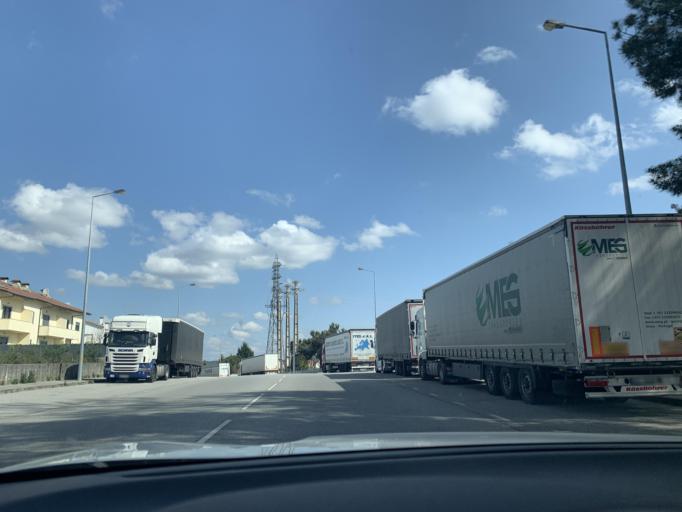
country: PT
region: Viseu
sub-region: Viseu
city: Rio de Loba
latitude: 40.6573
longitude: -7.8812
